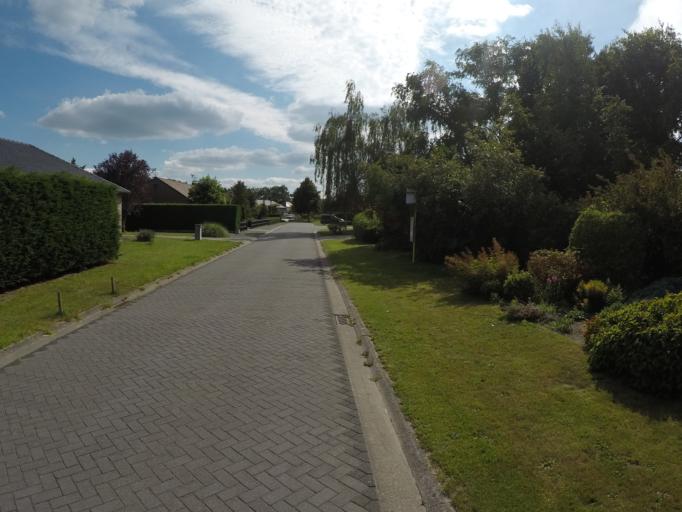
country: BE
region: Flanders
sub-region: Provincie Antwerpen
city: Nijlen
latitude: 51.1533
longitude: 4.6626
